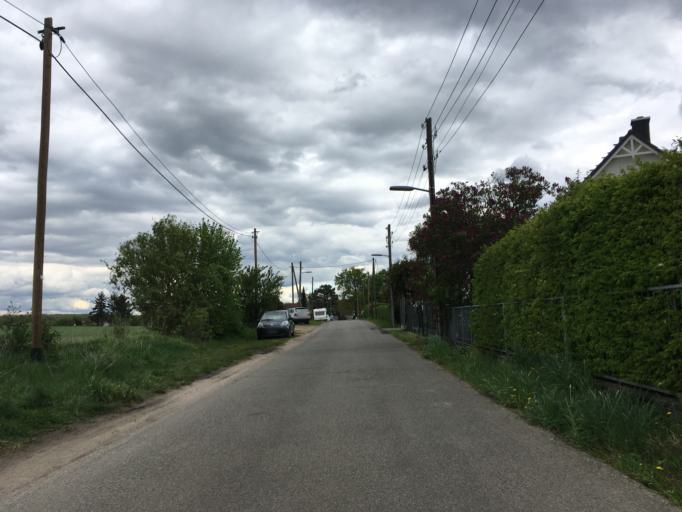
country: DE
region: Berlin
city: Blankenfelde
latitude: 52.6175
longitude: 13.4098
